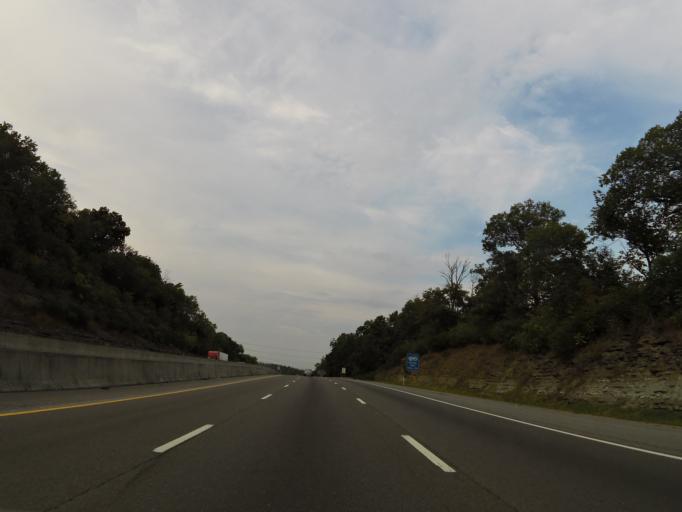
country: US
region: Tennessee
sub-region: Davidson County
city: Belle Meade
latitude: 36.1174
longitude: -86.9145
